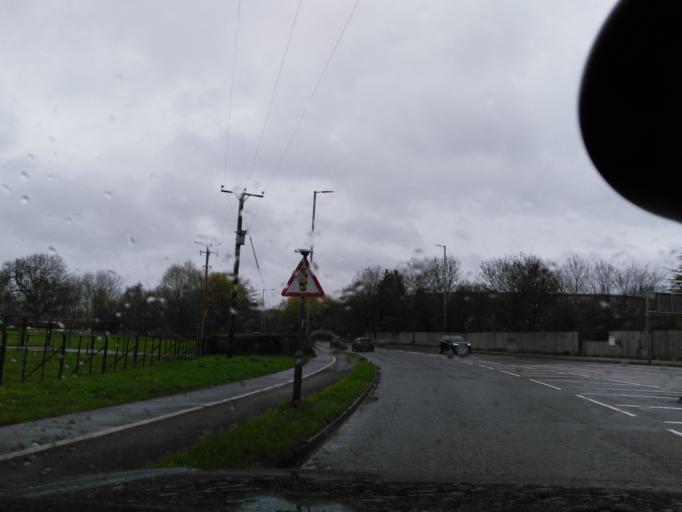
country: GB
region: England
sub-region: Somerset
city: Street
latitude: 51.1239
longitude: -2.7547
